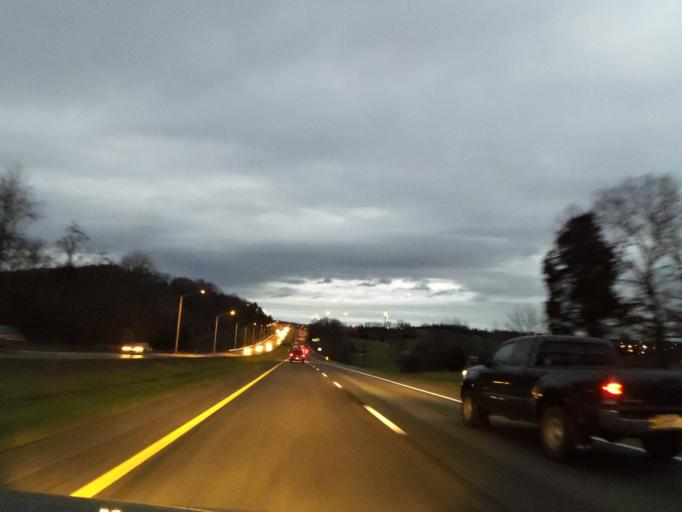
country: US
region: Tennessee
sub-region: Washington County
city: Gray
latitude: 36.4020
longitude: -82.4676
